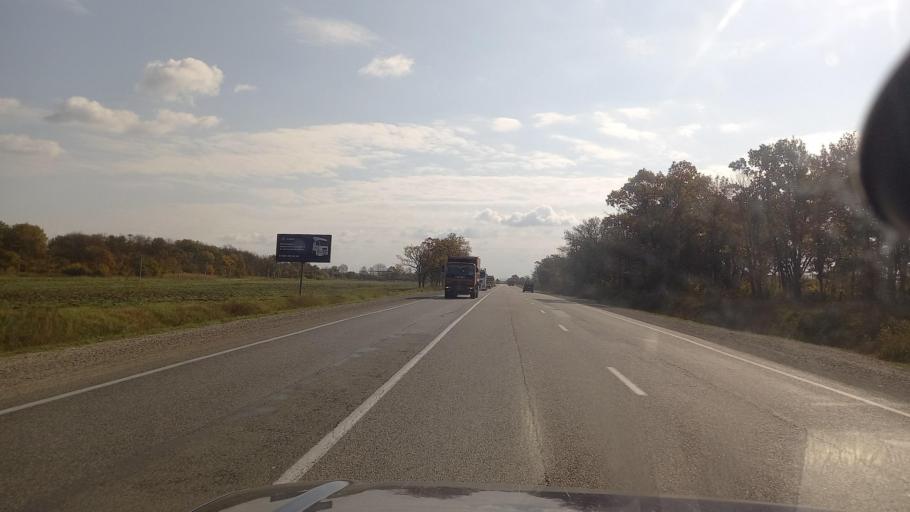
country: RU
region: Krasnodarskiy
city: Abinsk
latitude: 44.8775
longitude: 38.1057
